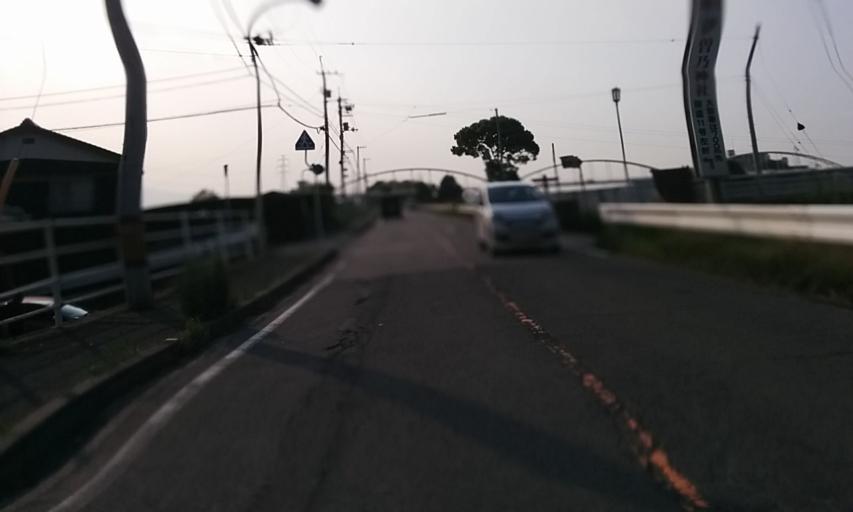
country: JP
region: Ehime
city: Saijo
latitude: 33.8993
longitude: 133.1895
